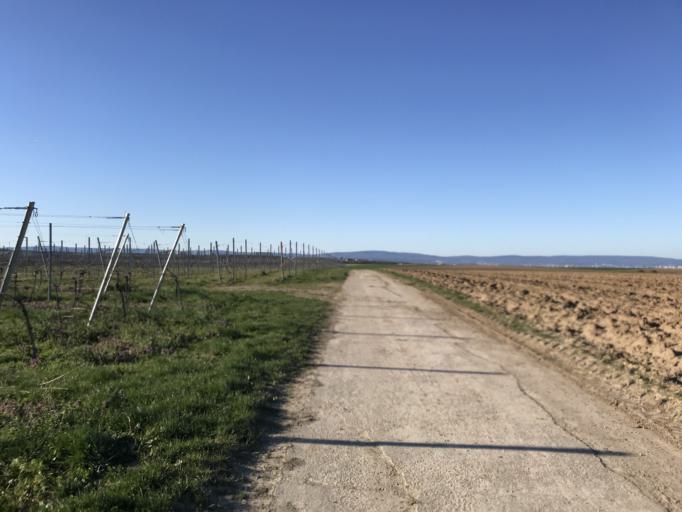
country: DE
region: Rheinland-Pfalz
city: Klein-Winternheim
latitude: 49.9334
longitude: 8.2335
